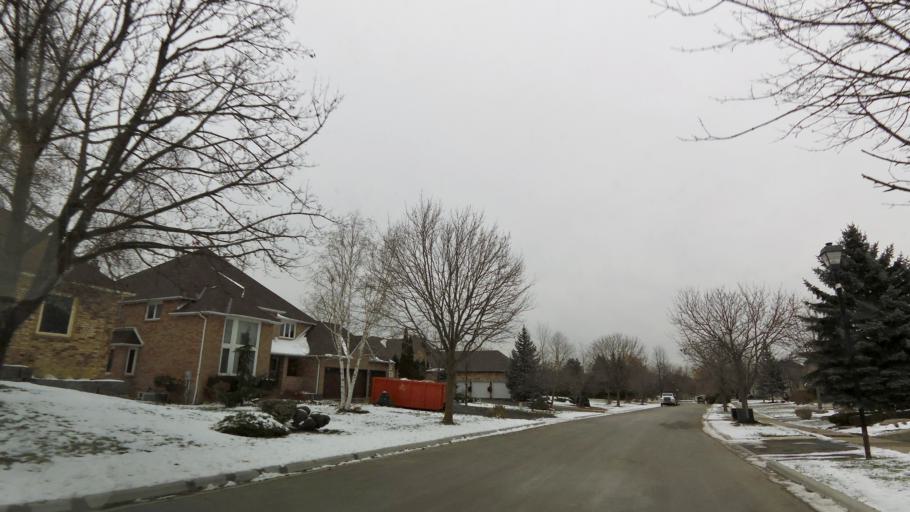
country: CA
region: Ontario
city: Vaughan
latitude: 43.8977
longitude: -79.6595
